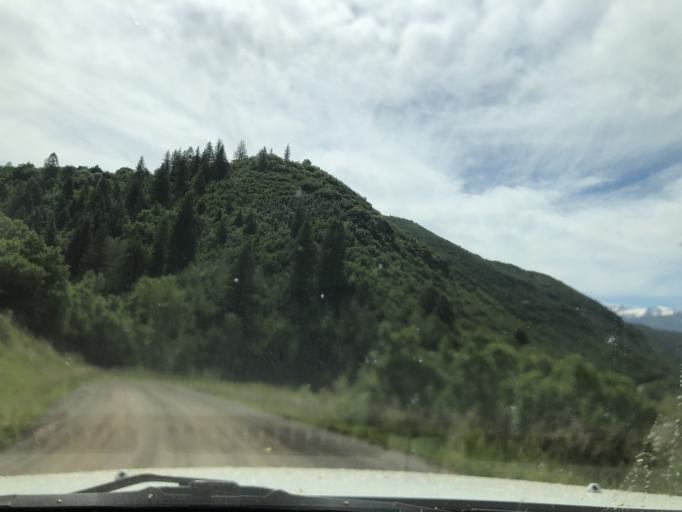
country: US
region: Colorado
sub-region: Delta County
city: Paonia
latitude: 38.9939
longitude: -107.3515
